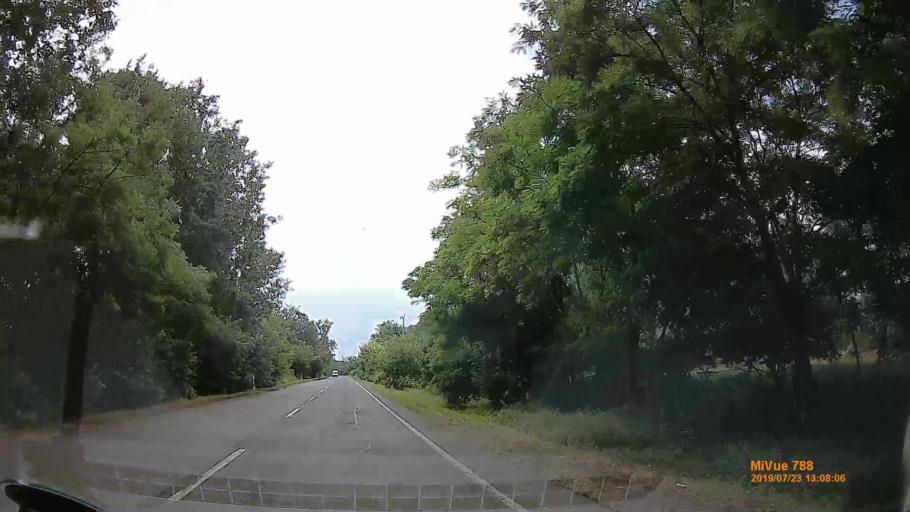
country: HU
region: Szabolcs-Szatmar-Bereg
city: Tiszavasvari
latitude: 47.9490
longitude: 21.3274
